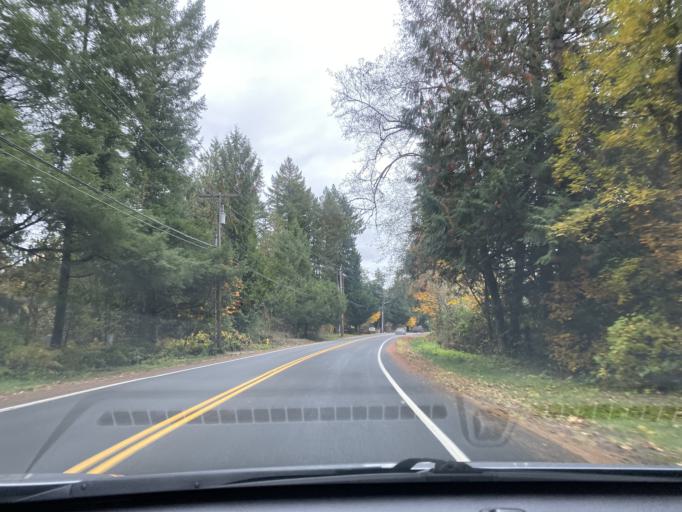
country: US
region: Washington
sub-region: King County
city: Lake Morton-Berrydale
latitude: 47.3023
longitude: -122.1166
